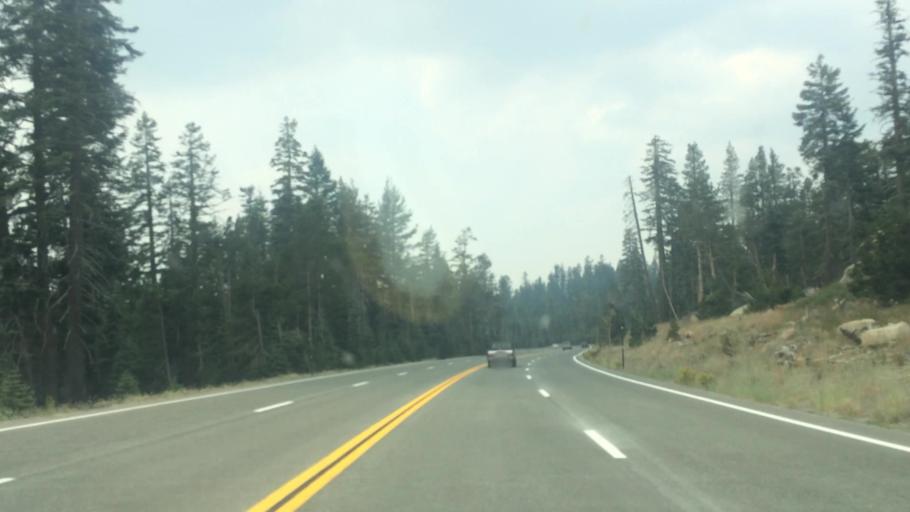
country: US
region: California
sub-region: El Dorado County
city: South Lake Tahoe
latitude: 38.6310
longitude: -120.1872
